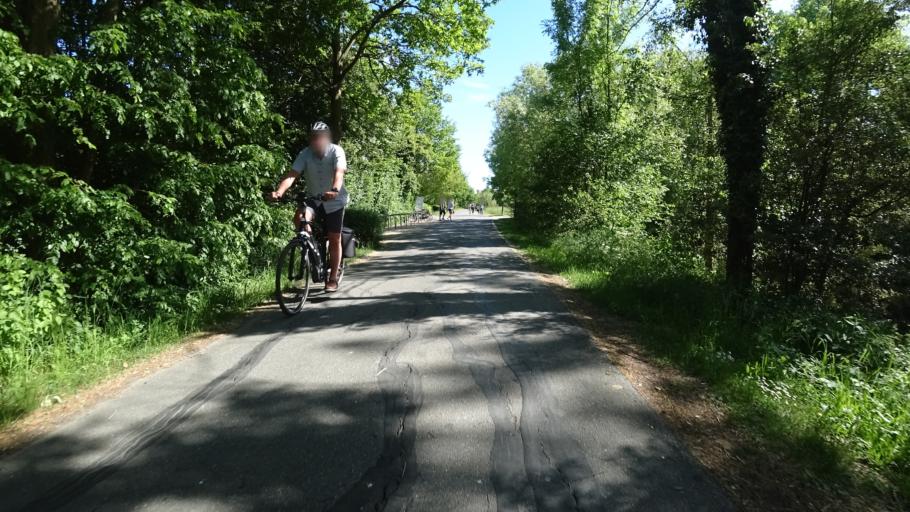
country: DE
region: North Rhine-Westphalia
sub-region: Regierungsbezirk Detmold
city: Rheda-Wiedenbruck
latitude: 51.8214
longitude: 8.2306
